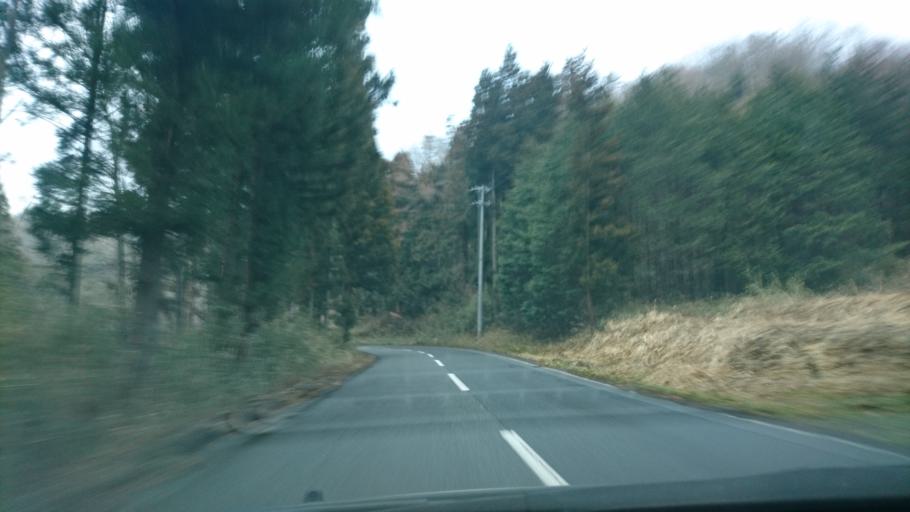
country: JP
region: Iwate
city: Ichinoseki
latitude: 39.0169
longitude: 141.3656
